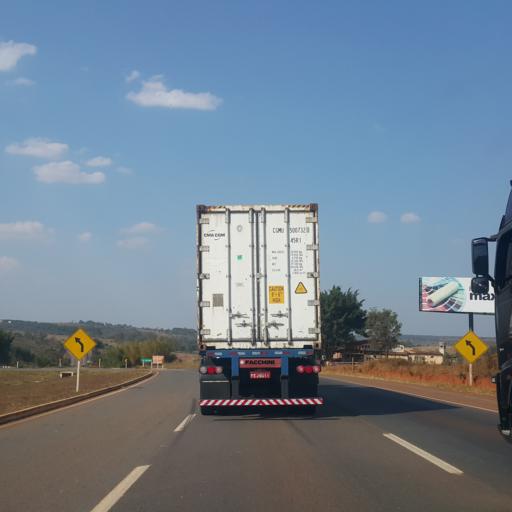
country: BR
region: Goias
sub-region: Abadiania
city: Abadiania
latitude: -16.3004
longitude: -48.8114
